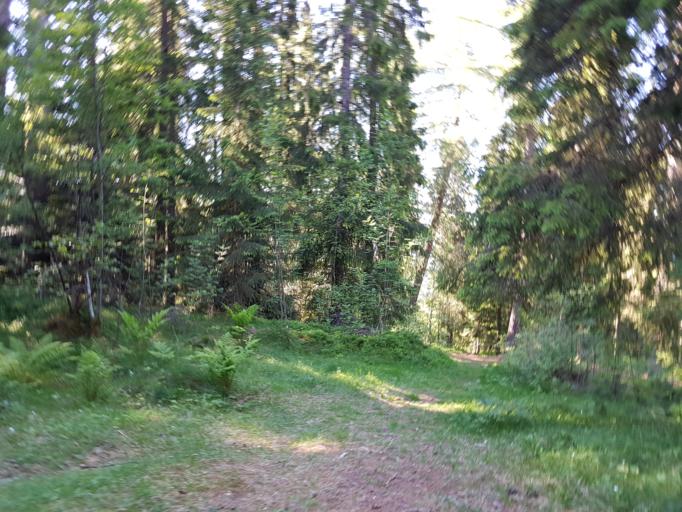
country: NO
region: Sor-Trondelag
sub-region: Trondheim
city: Trondheim
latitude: 63.4224
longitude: 10.3626
